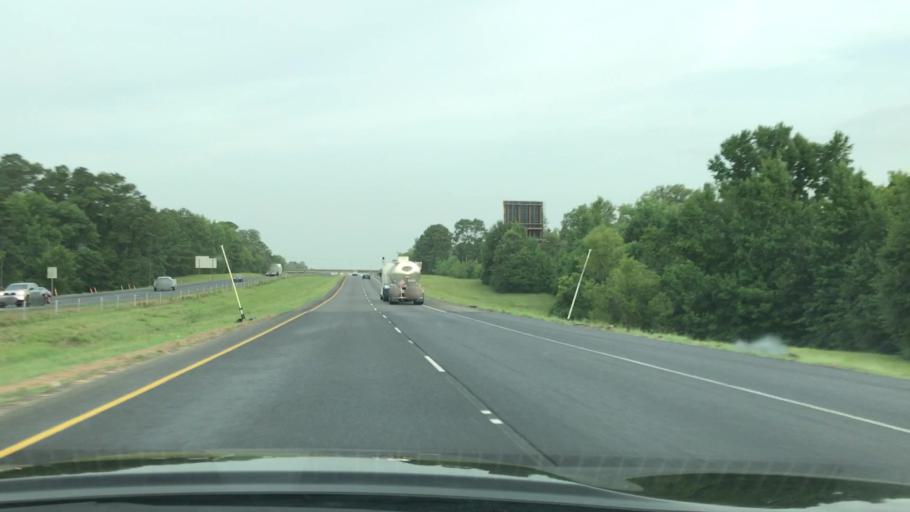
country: US
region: Louisiana
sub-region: Caddo Parish
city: Greenwood
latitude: 32.4518
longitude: -94.0045
